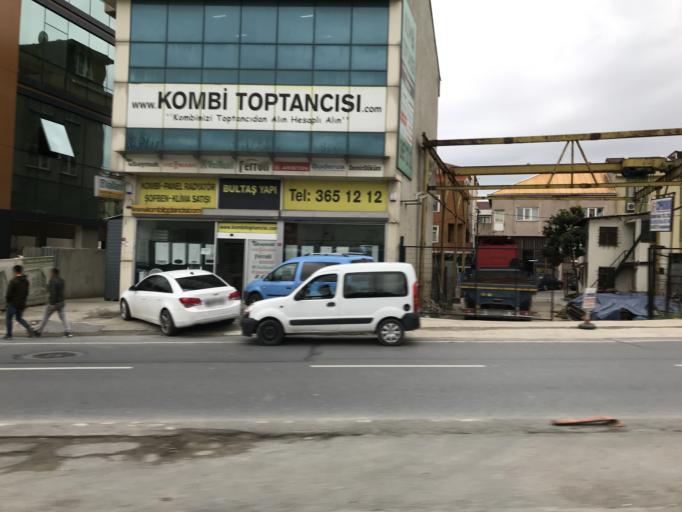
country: TR
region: Istanbul
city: Umraniye
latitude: 41.0118
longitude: 29.1645
